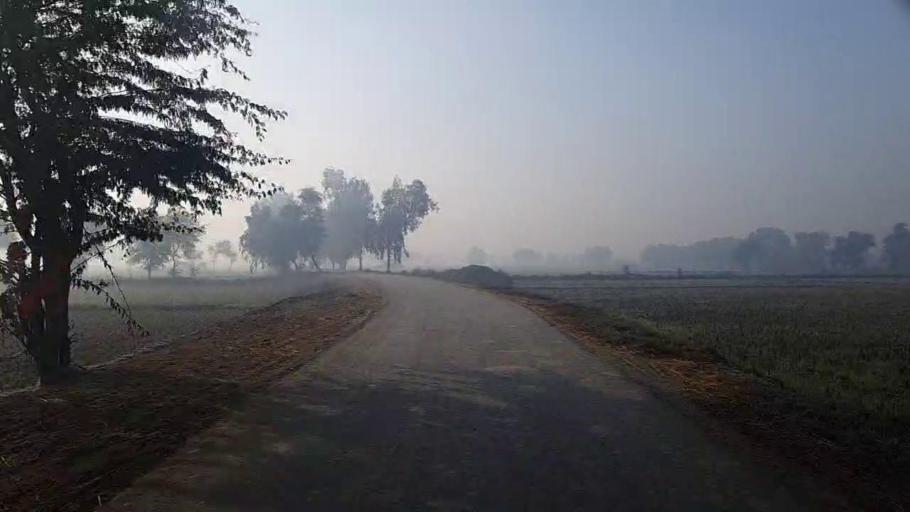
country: PK
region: Sindh
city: Mehar
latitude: 27.1440
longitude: 67.8227
